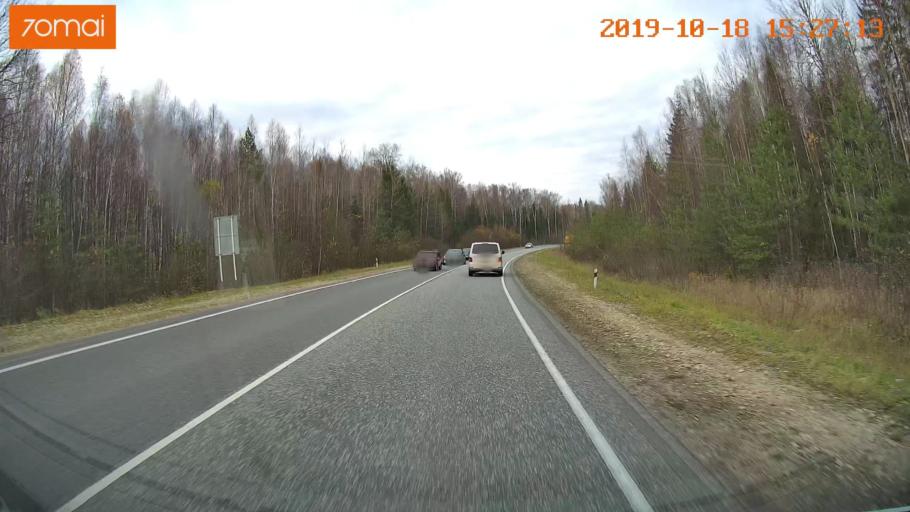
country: RU
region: Vladimir
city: Anopino
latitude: 55.7505
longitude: 40.6717
